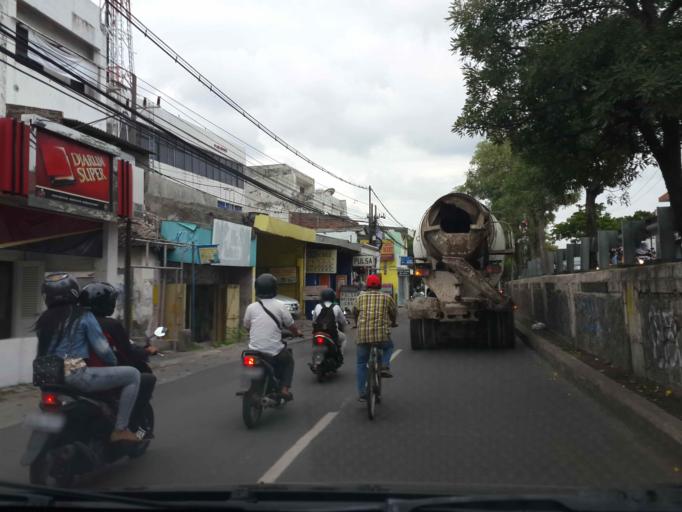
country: ID
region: East Java
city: Gubengairlangga
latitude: -7.2705
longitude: 112.7210
